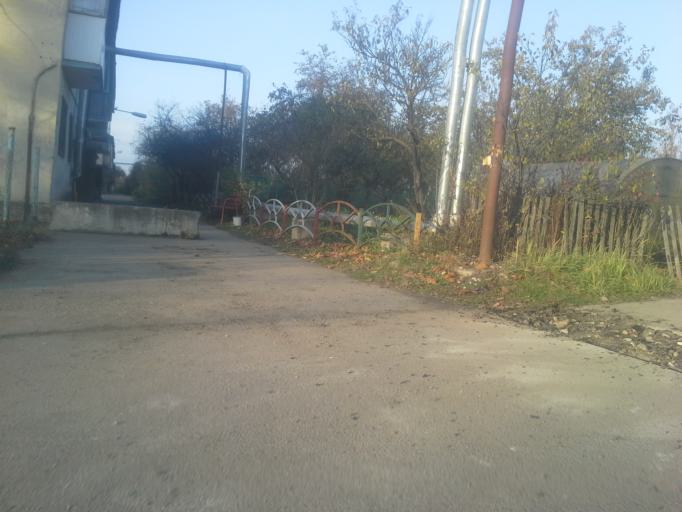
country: RU
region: Moskovskaya
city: Golitsyno
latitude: 55.6030
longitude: 36.9959
